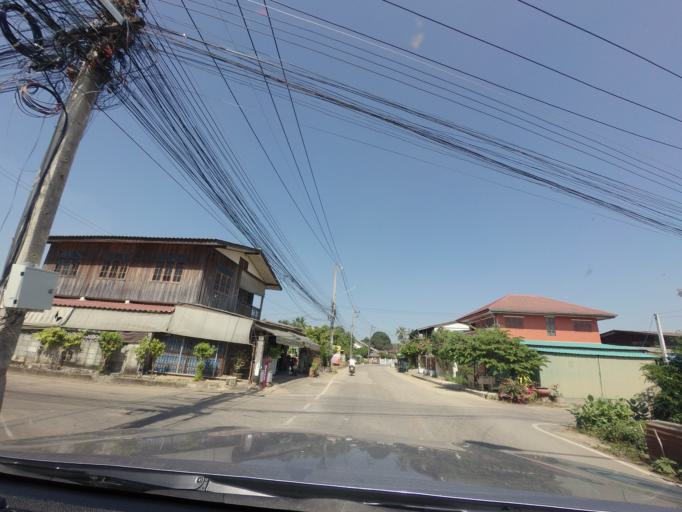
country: TH
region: Sukhothai
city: Sawankhalok
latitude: 17.3151
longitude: 99.8244
